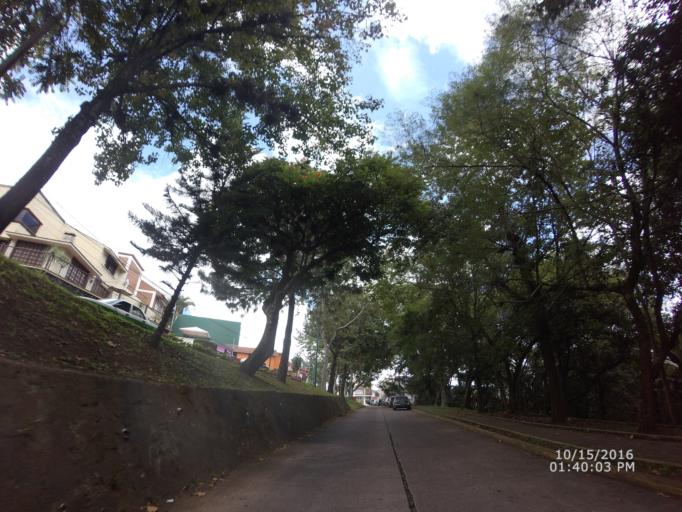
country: MX
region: Veracruz
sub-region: Xalapa
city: Xalapa de Enriquez
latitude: 19.5332
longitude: -96.8928
